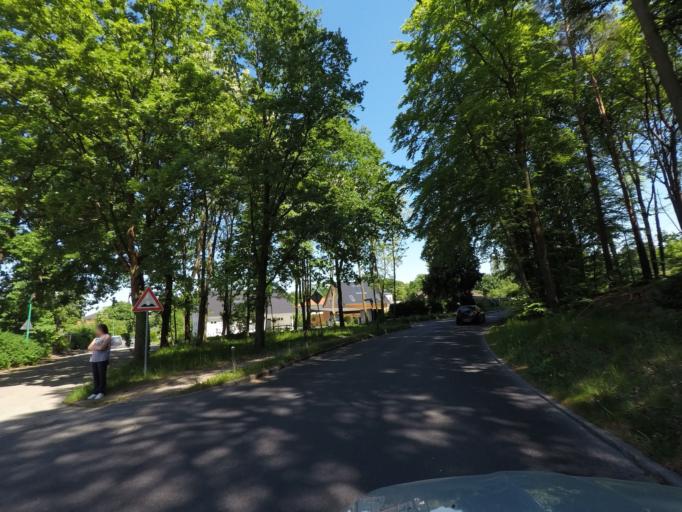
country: DE
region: Brandenburg
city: Eberswalde
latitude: 52.8277
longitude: 13.8258
